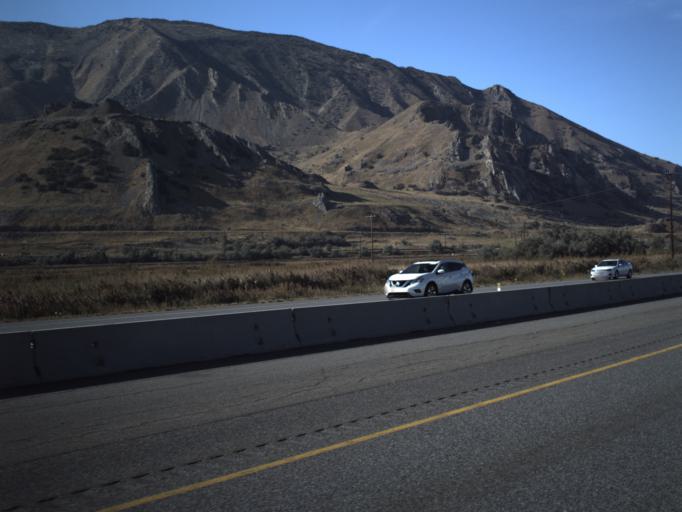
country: US
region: Utah
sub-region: Salt Lake County
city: Magna
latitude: 40.7286
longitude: -112.2124
